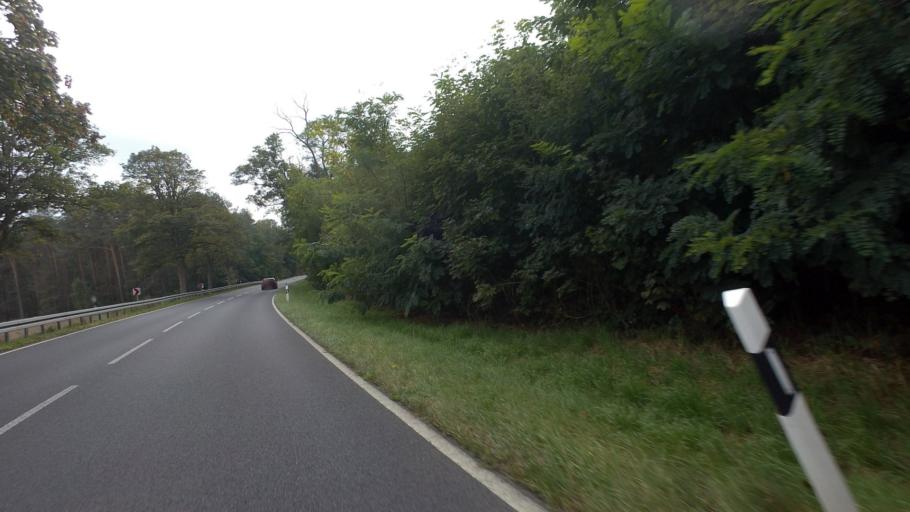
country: DE
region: Brandenburg
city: Sonnewalde
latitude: 51.7435
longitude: 13.6814
